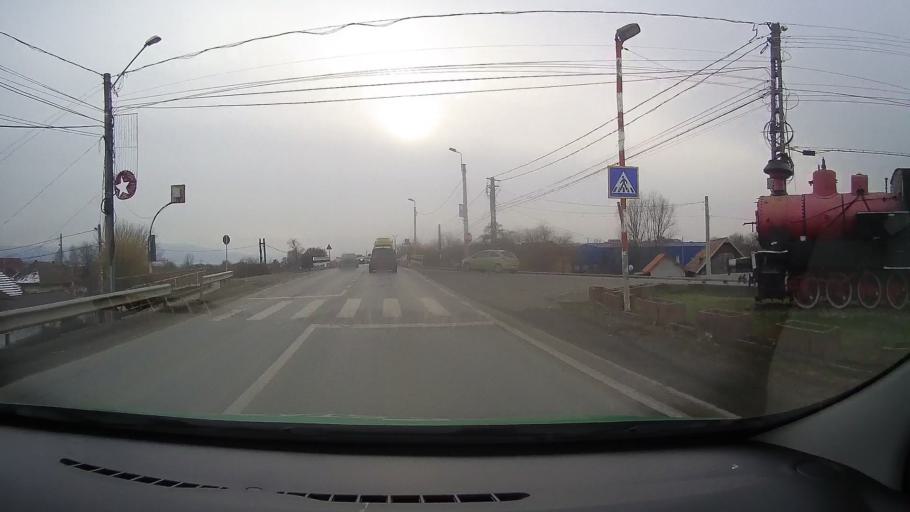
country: RO
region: Hunedoara
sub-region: Municipiul Orastie
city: Orastie
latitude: 45.8555
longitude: 23.2091
